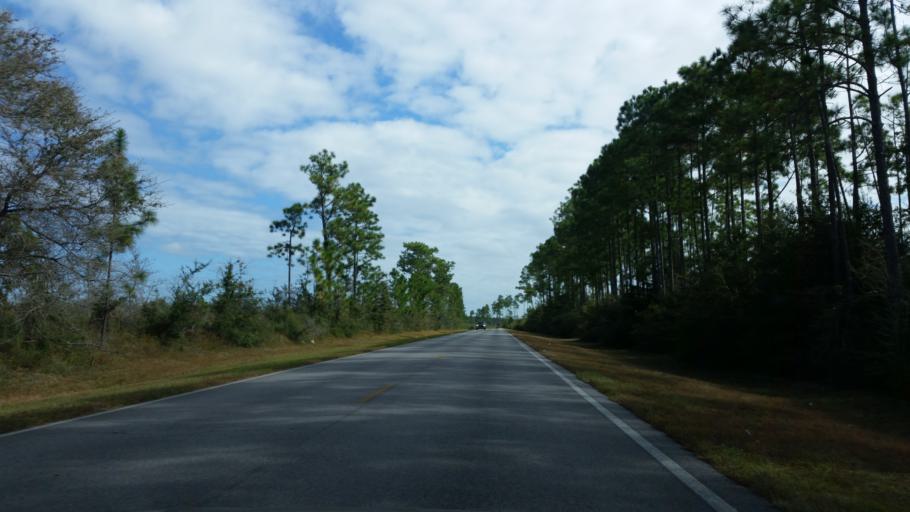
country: US
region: Florida
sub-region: Santa Rosa County
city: Point Baker
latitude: 30.7235
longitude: -86.9573
